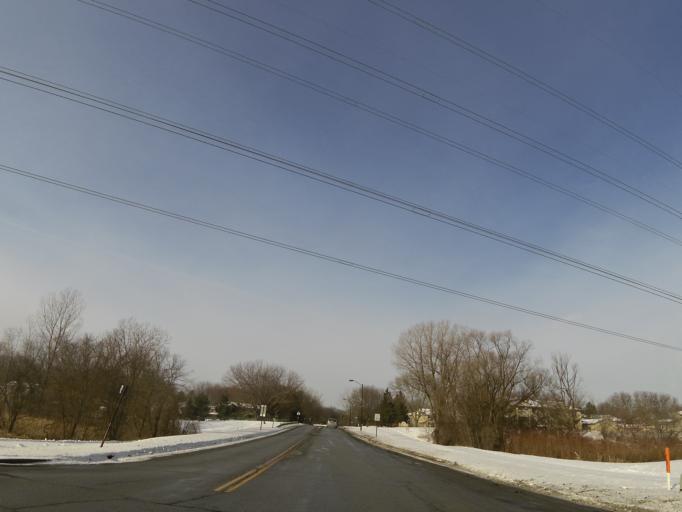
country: US
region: Minnesota
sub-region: Hennepin County
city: Eden Prairie
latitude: 44.8421
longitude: -93.4296
